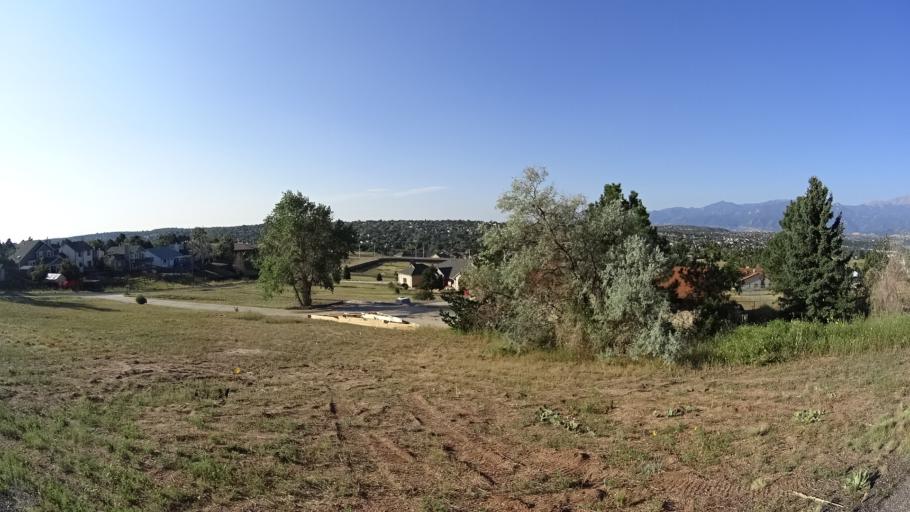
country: US
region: Colorado
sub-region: El Paso County
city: Black Forest
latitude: 38.9386
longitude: -104.7667
